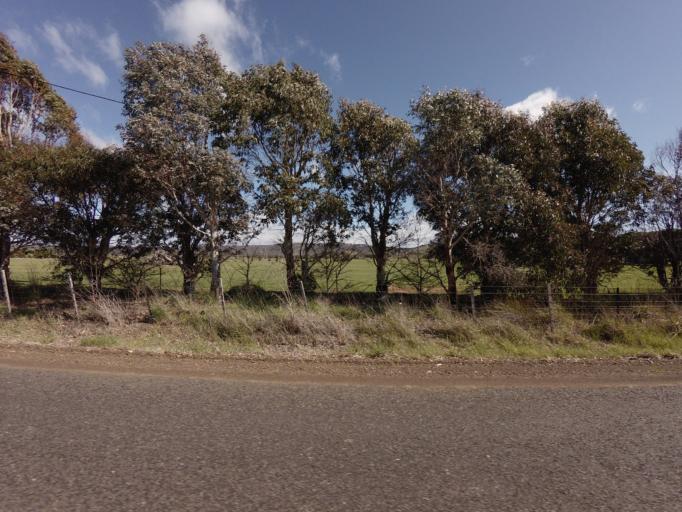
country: AU
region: Tasmania
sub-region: Northern Midlands
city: Evandale
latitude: -42.0085
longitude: 147.4586
